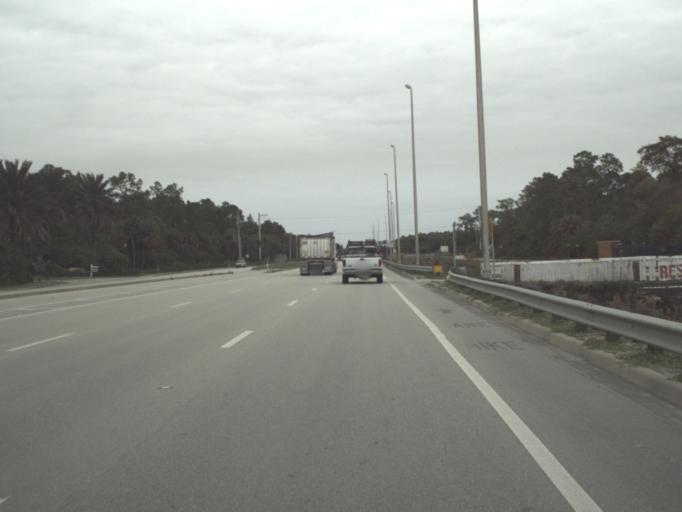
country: US
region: Florida
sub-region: Collier County
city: Lely Resort
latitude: 26.1253
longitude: -81.6869
